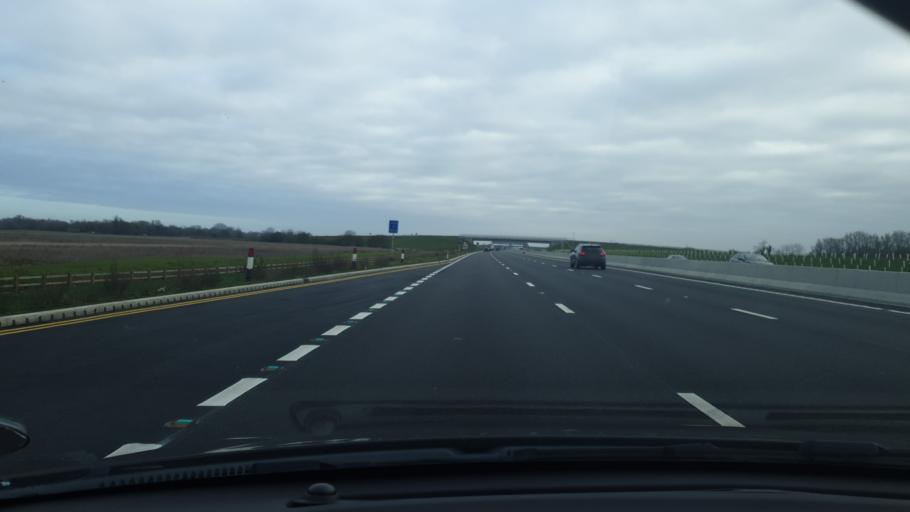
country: GB
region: England
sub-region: Cambridgeshire
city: Hemingford Grey
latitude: 52.2925
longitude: -0.1080
